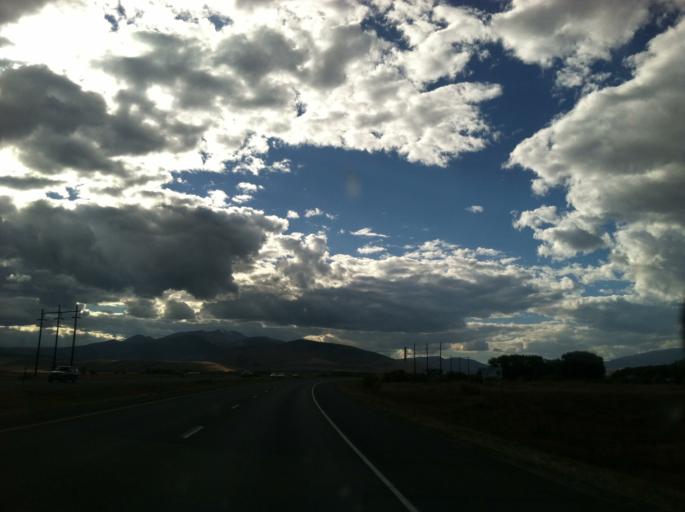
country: US
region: Montana
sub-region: Deer Lodge County
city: Warm Springs
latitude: 46.0959
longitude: -112.8219
